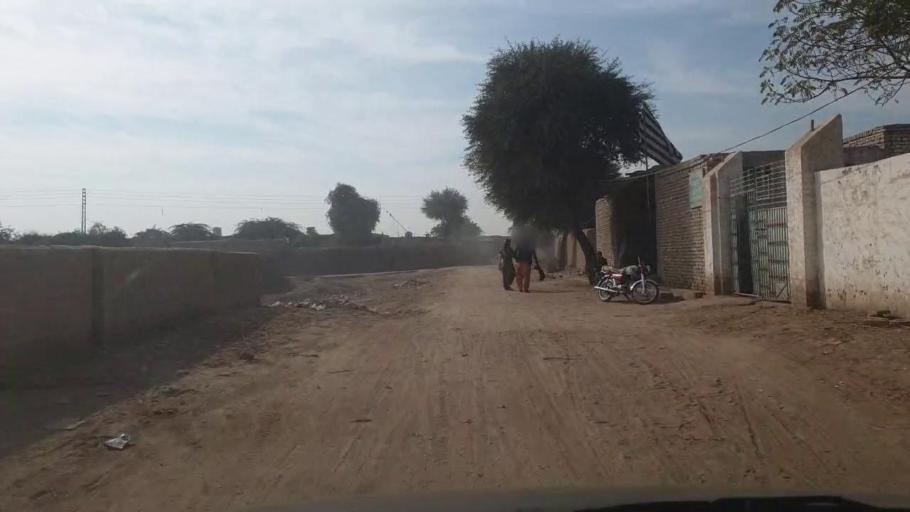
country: PK
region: Sindh
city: Shahpur Chakar
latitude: 26.1765
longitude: 68.5931
